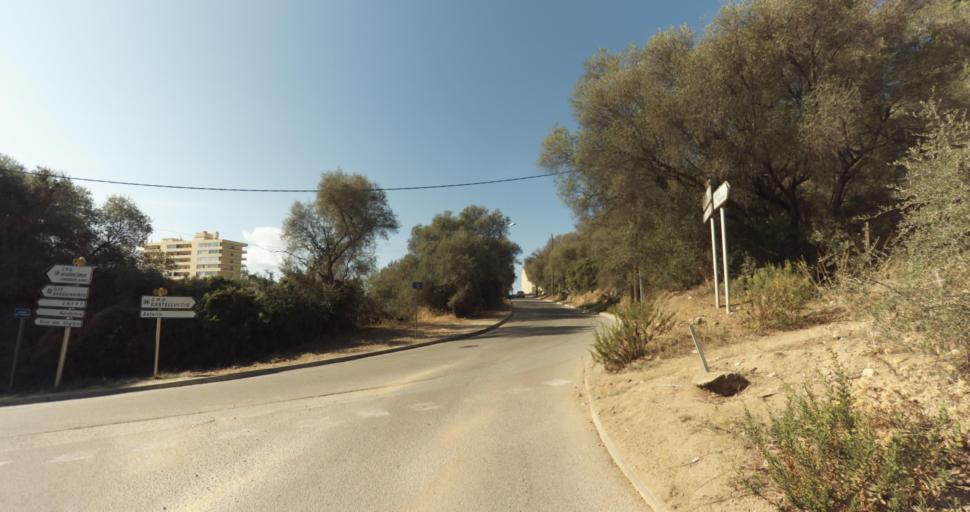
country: FR
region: Corsica
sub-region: Departement de la Corse-du-Sud
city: Ajaccio
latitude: 41.9233
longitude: 8.7304
